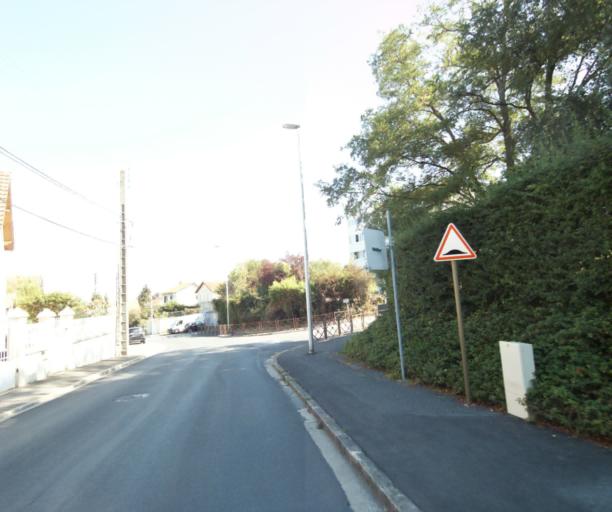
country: FR
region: Ile-de-France
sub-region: Departement de Seine-et-Marne
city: Gouvernes
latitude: 48.8696
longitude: 2.7009
